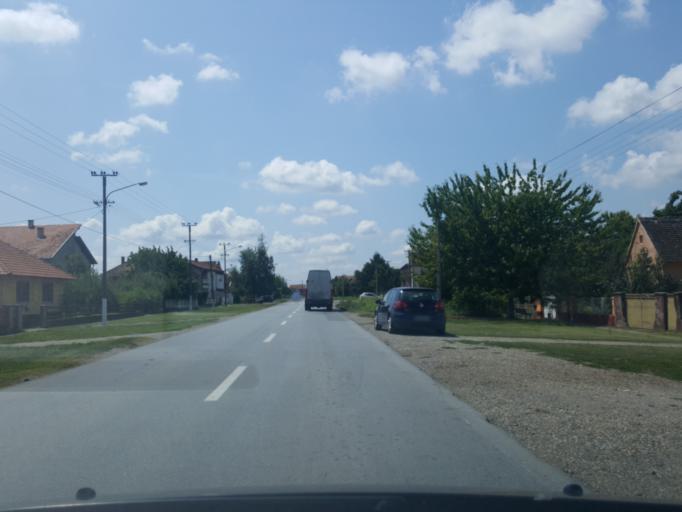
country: RS
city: Salas Nocajski
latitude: 44.9527
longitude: 19.5951
